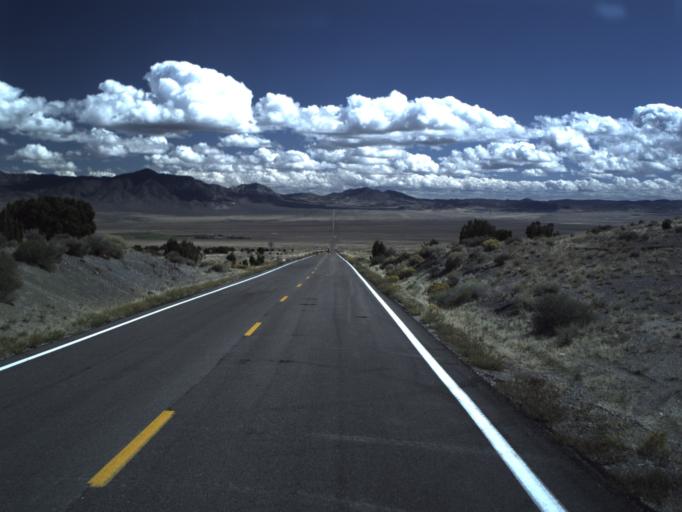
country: US
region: Utah
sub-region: Beaver County
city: Milford
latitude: 38.5031
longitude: -113.5071
